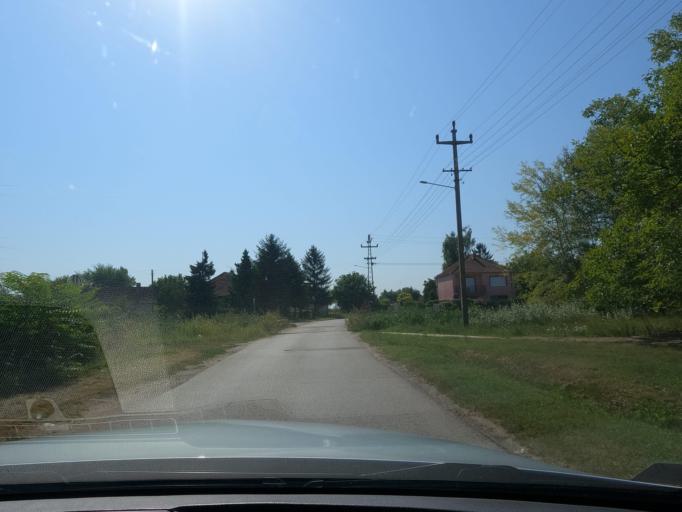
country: HU
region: Csongrad
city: Asotthalom
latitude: 46.0994
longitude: 19.7784
